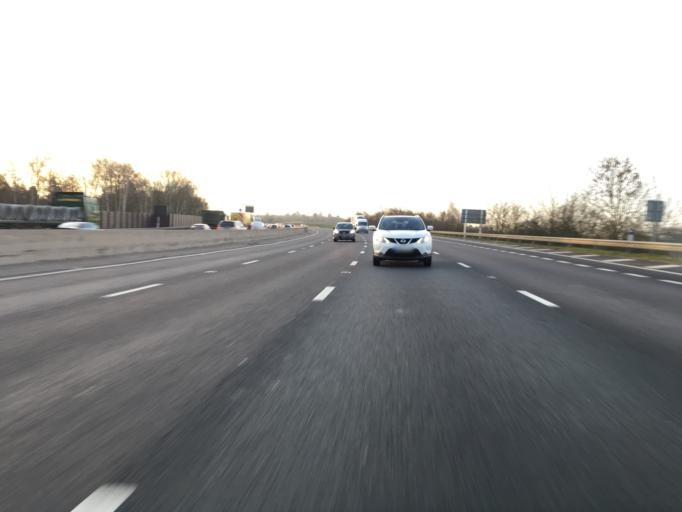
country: GB
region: England
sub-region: Worcestershire
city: Droitwich
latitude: 52.2919
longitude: -2.1213
